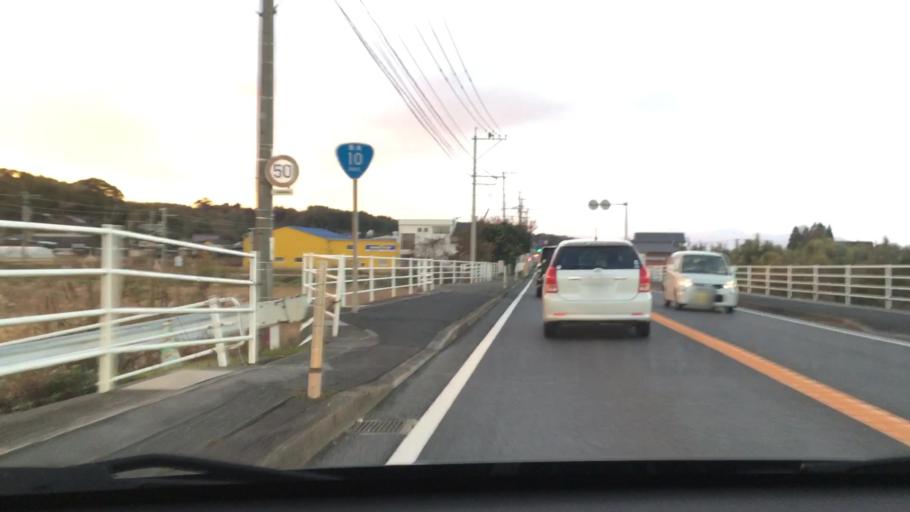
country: JP
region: Fukuoka
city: Shiida
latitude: 33.6315
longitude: 131.0821
